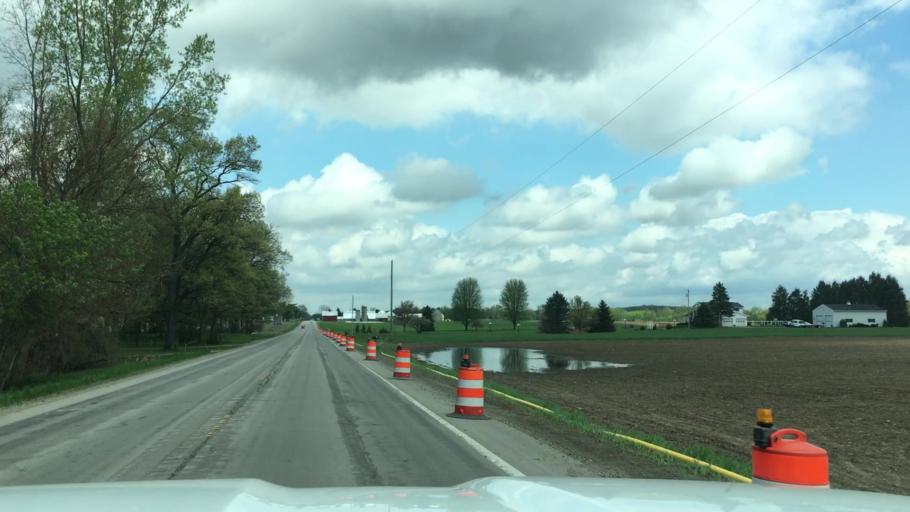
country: US
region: Michigan
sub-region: Ingham County
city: Stockbridge
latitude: 42.4593
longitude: -84.1901
